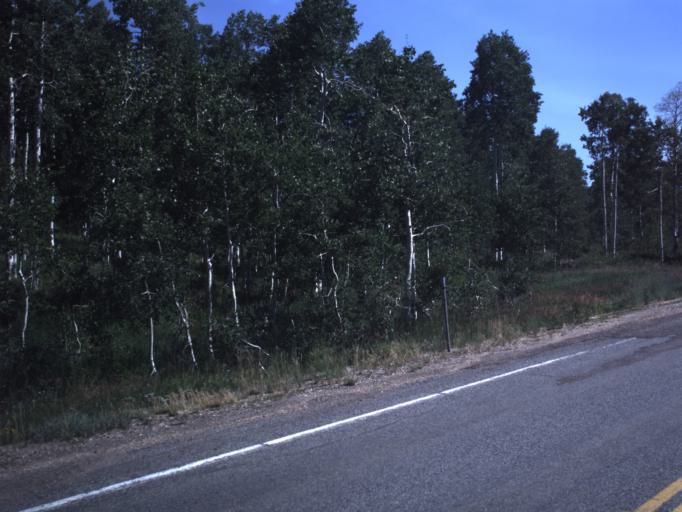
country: US
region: Utah
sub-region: Sanpete County
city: Fairview
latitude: 39.6786
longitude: -111.3173
